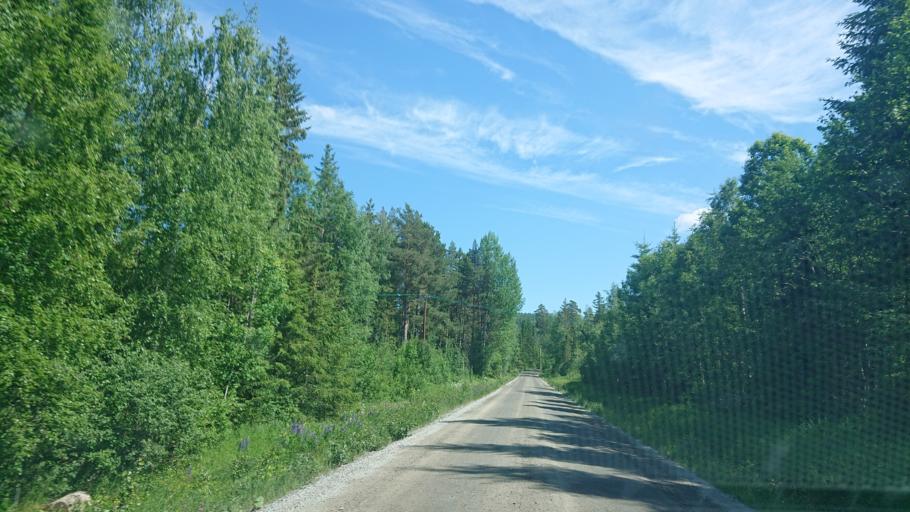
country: SE
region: Vaesternorrland
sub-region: Solleftea Kommun
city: Solleftea
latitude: 62.9700
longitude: 17.1756
